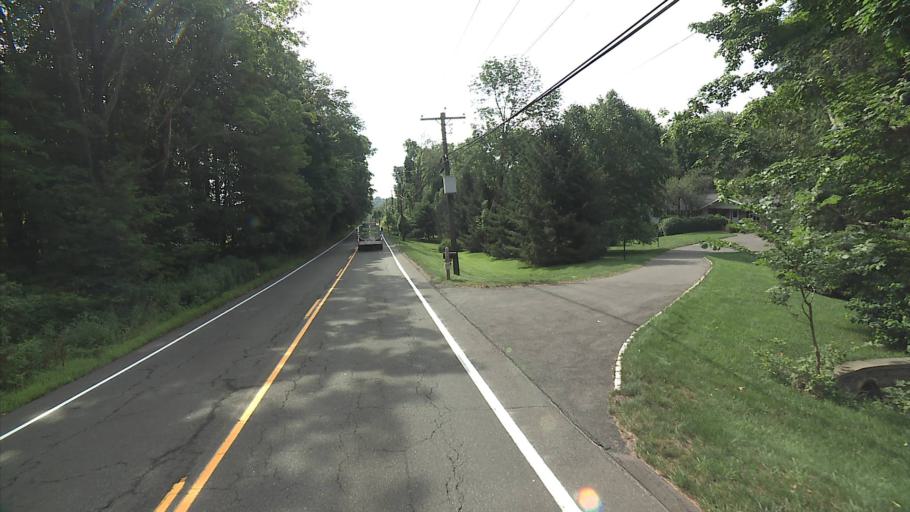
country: US
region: Connecticut
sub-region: New Haven County
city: Woodbridge
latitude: 41.3511
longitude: -73.0311
